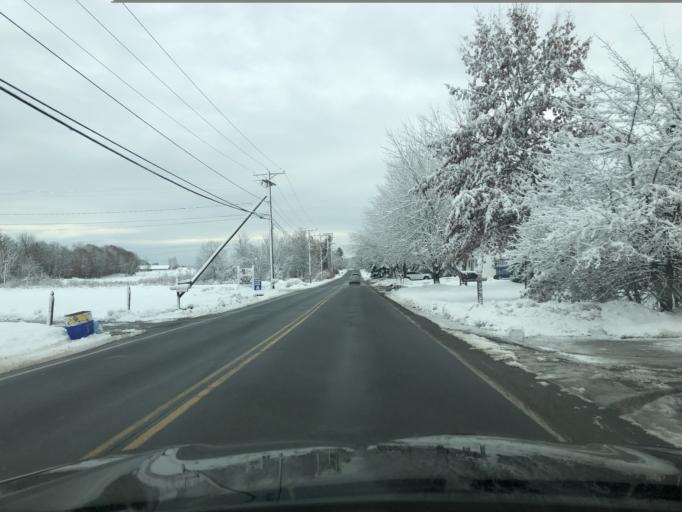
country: US
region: New Hampshire
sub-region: Strafford County
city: Somersworth
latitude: 43.2484
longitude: -70.8628
